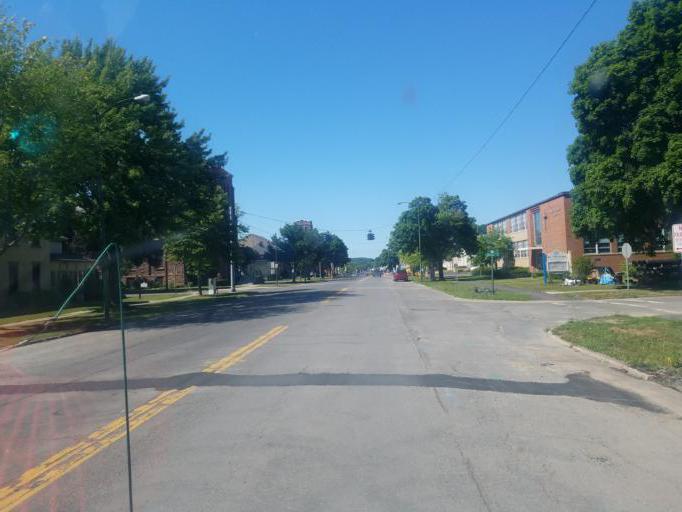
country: US
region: New York
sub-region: Wayne County
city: Newark
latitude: 43.0424
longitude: -77.0956
